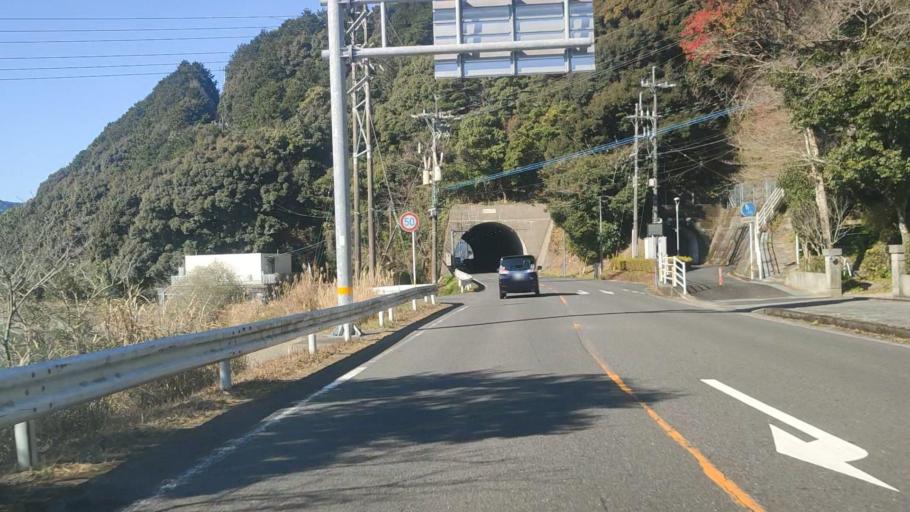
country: JP
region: Oita
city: Saiki
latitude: 32.9420
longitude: 131.9097
